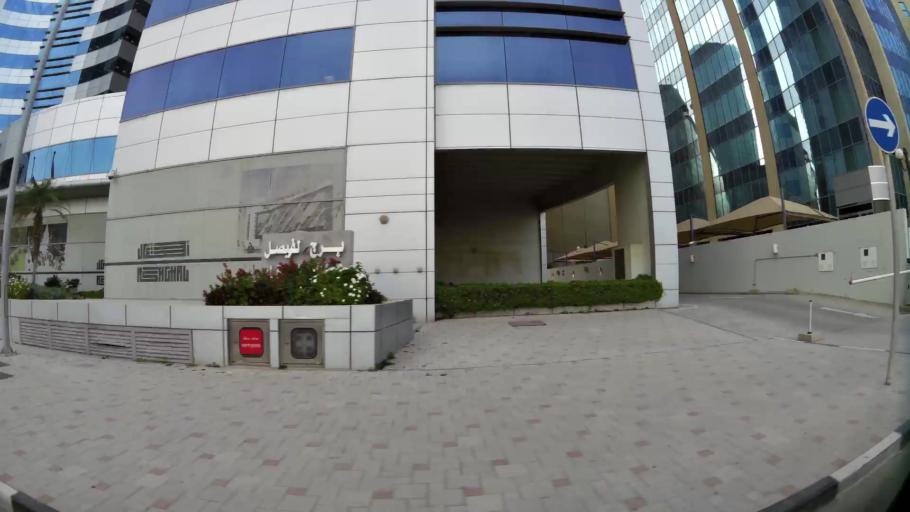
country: QA
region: Baladiyat ad Dawhah
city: Doha
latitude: 25.3213
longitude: 51.5312
